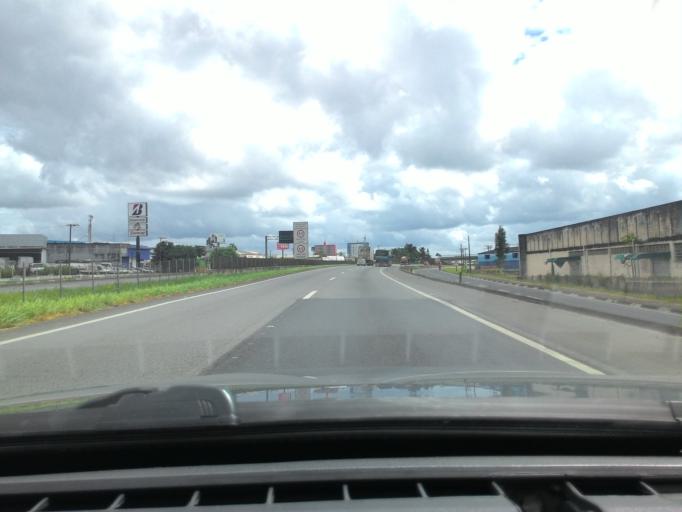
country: BR
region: Sao Paulo
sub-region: Registro
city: Registro
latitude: -24.5043
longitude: -47.8476
